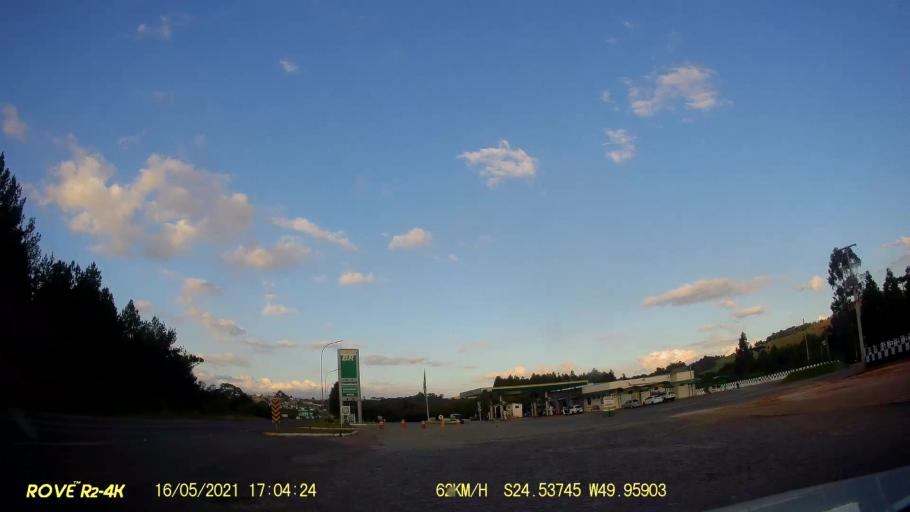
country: BR
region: Parana
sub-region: Pirai Do Sul
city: Pirai do Sul
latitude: -24.5377
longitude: -49.9589
